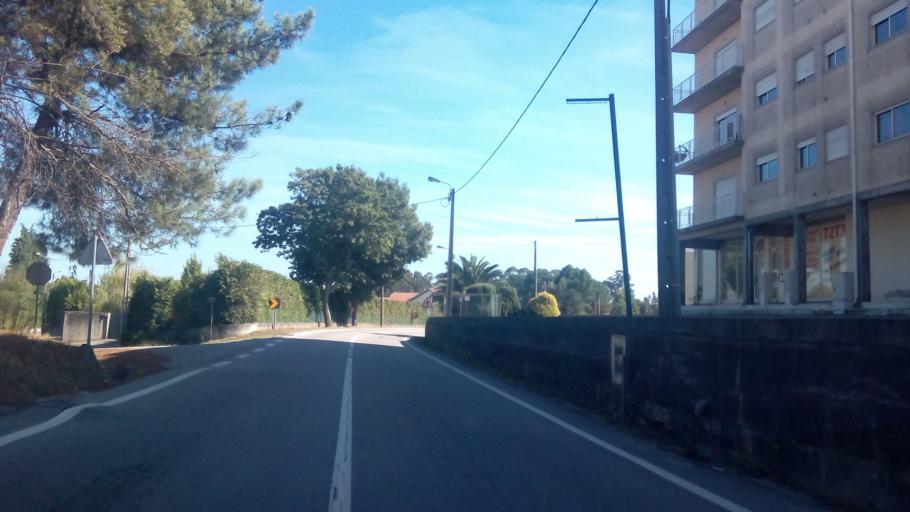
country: PT
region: Porto
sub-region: Paredes
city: Baltar
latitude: 41.1789
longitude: -8.3872
